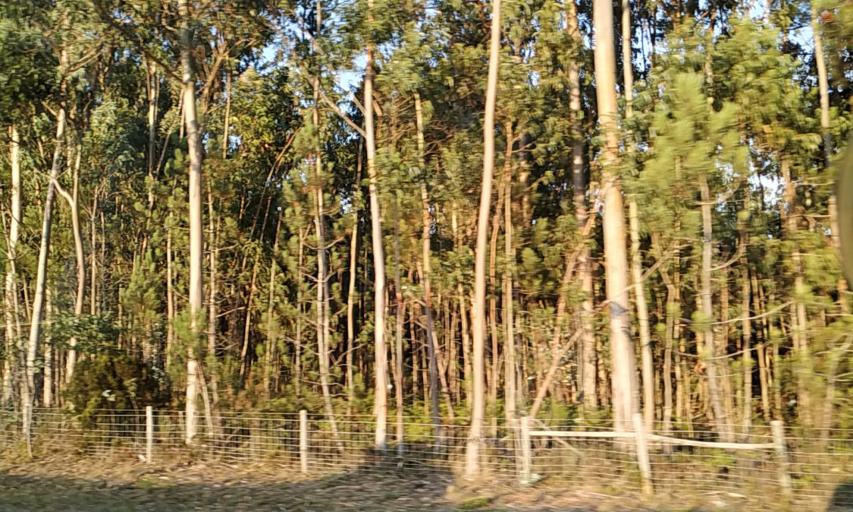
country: PT
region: Santarem
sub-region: Ourem
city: Fatima
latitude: 39.6315
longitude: -8.6983
